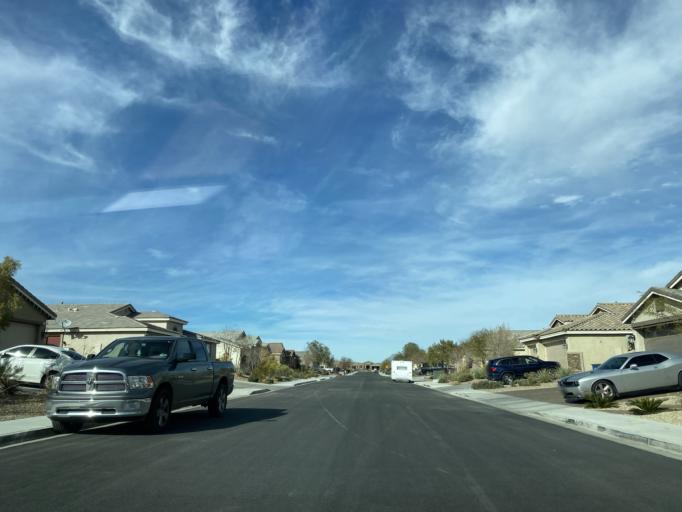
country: US
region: Nevada
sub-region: Clark County
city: Summerlin South
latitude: 36.2702
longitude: -115.3269
